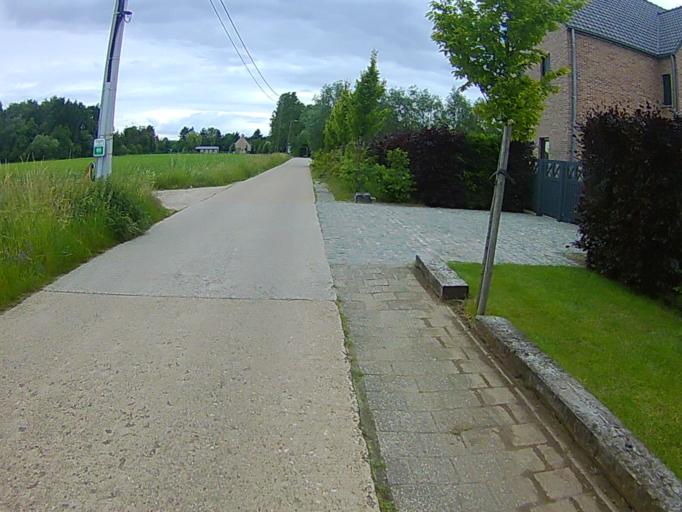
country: BE
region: Flanders
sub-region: Provincie Antwerpen
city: Putte
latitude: 51.0453
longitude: 4.6501
